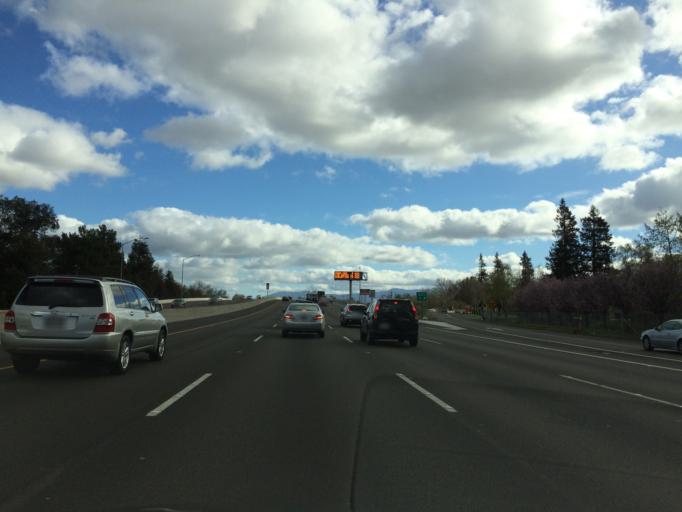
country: US
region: California
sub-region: Santa Clara County
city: Milpitas
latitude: 37.3858
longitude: -121.9054
